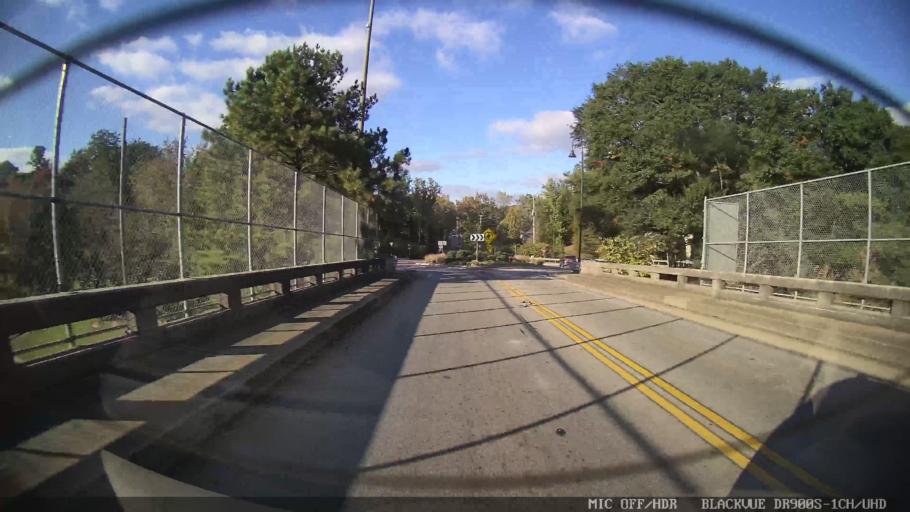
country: US
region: Georgia
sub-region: Fulton County
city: Sandy Springs
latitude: 33.9153
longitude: -84.3925
